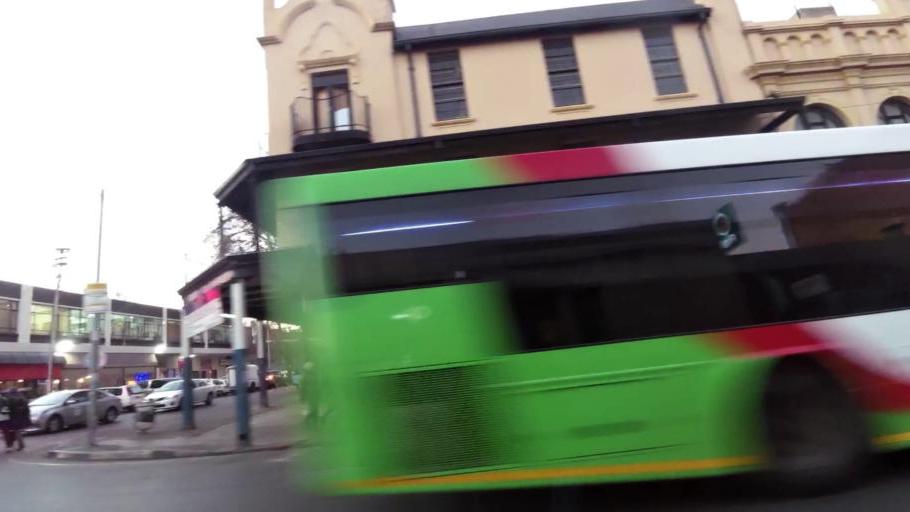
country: ZA
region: Gauteng
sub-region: City of Johannesburg Metropolitan Municipality
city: Johannesburg
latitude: -26.2054
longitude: 28.0206
